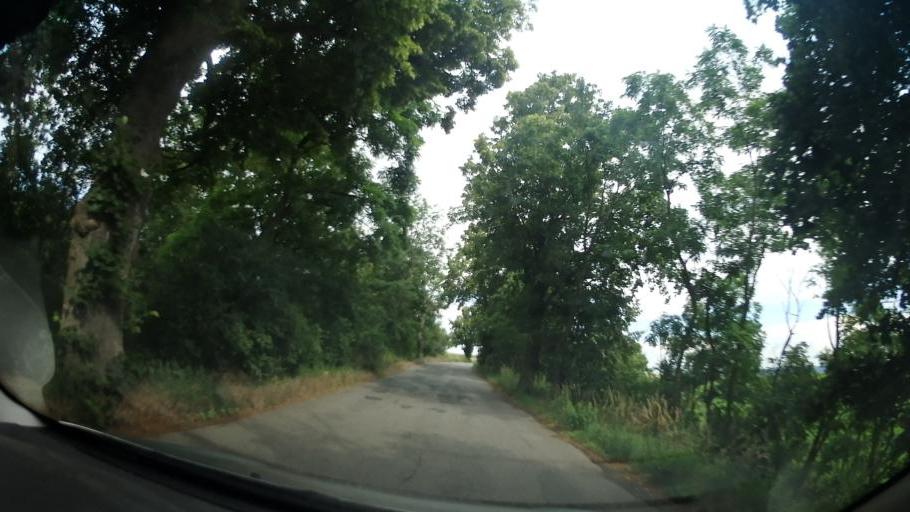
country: CZ
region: South Moravian
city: Oslavany
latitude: 49.1299
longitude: 16.3564
